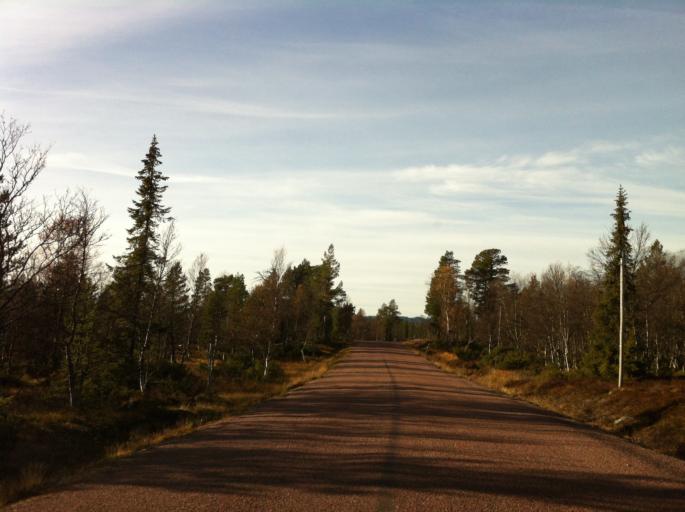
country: NO
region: Hedmark
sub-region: Engerdal
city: Engerdal
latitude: 62.0715
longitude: 12.1993
